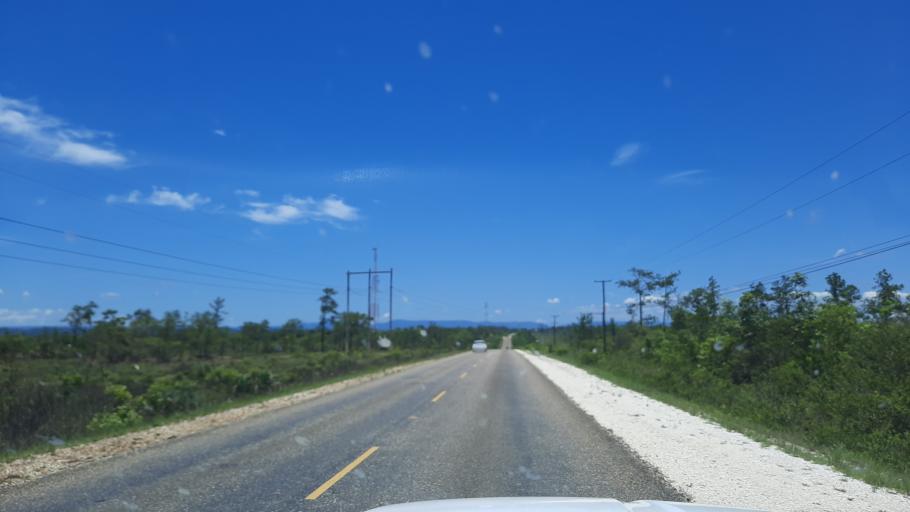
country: BZ
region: Cayo
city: Belmopan
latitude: 17.3505
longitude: -88.5524
